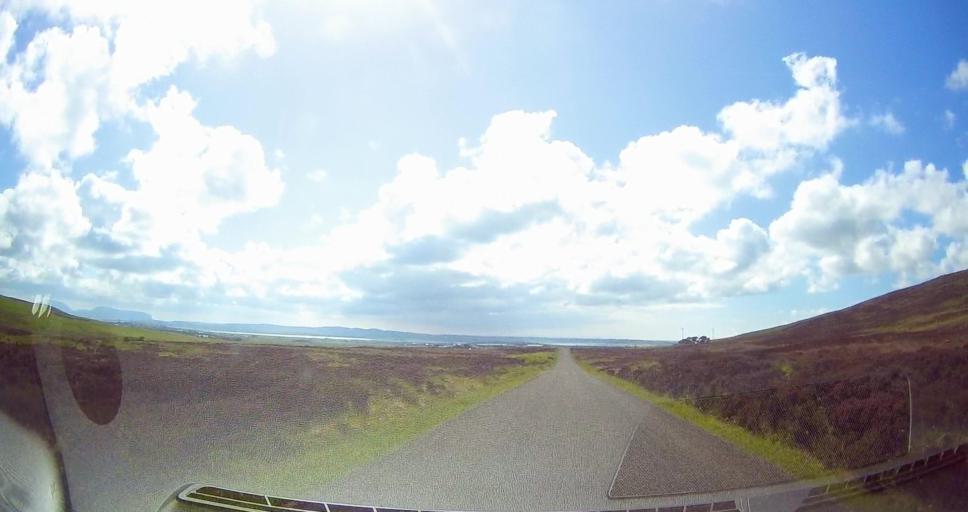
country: GB
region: Scotland
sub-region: Orkney Islands
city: Stromness
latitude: 59.0472
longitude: -3.1348
